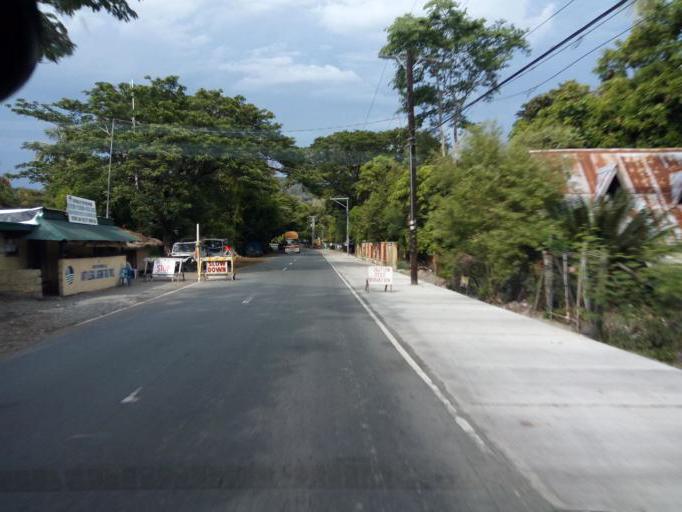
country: PH
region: Central Luzon
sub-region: Province of Nueva Ecija
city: Tayabo
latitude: 15.8298
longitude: 121.0298
